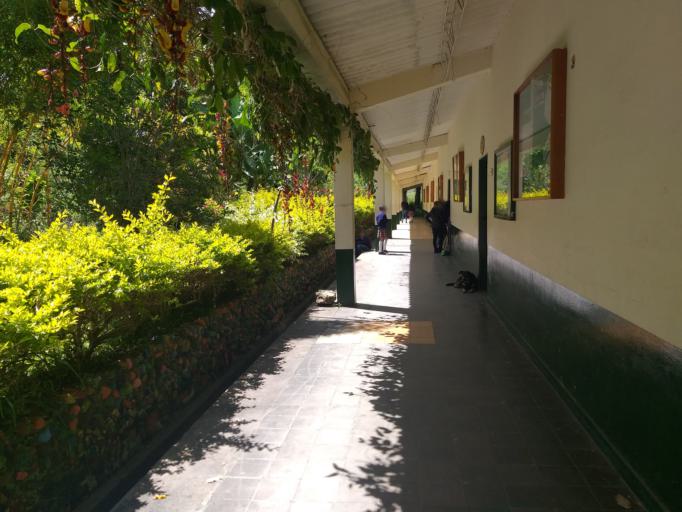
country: CO
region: Boyaca
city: Boavita
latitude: 6.3267
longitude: -72.5796
